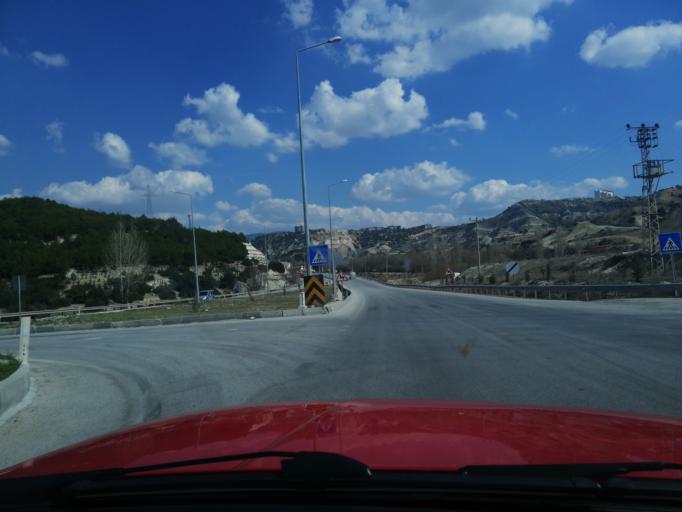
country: TR
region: Burdur
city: Burdur
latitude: 37.6998
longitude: 30.3195
